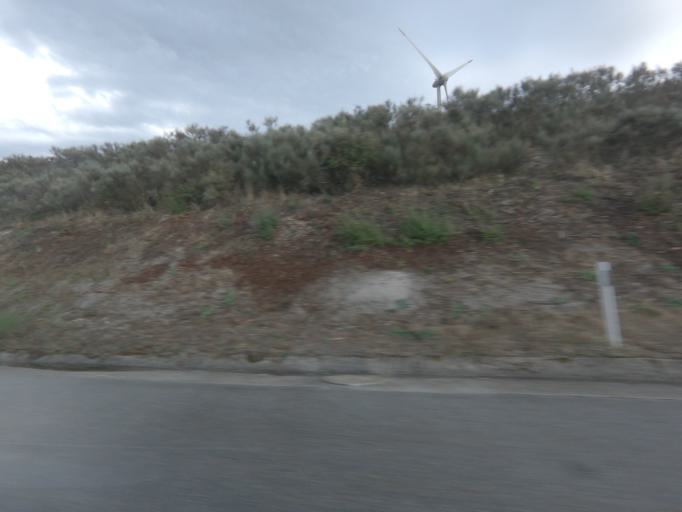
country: PT
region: Viseu
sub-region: Tarouca
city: Tarouca
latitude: 41.0266
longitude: -7.8713
